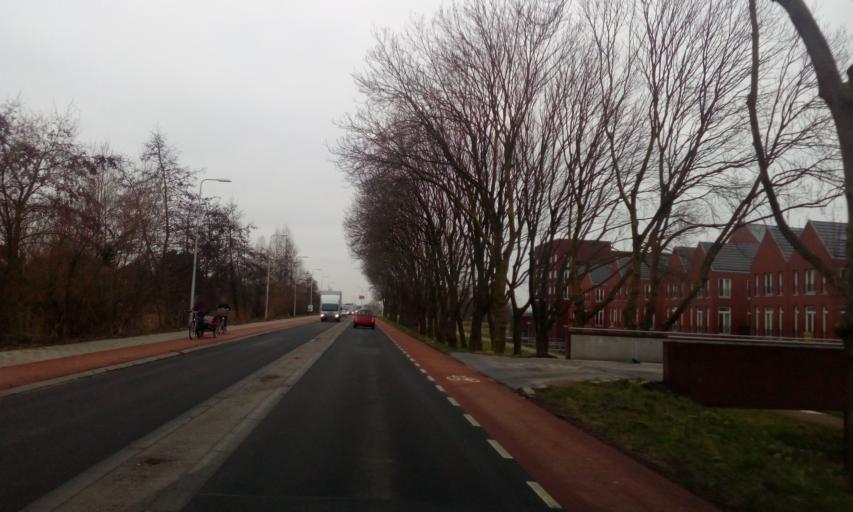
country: NL
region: South Holland
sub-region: Gemeente Waddinxveen
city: Waddinxveen
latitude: 52.0419
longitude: 4.6534
